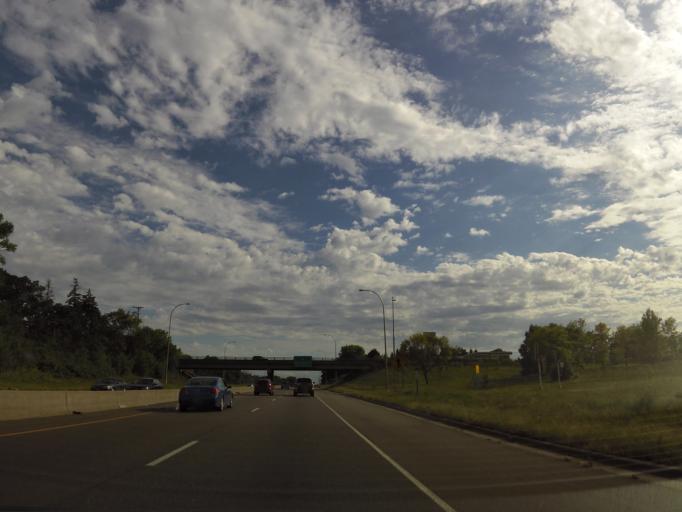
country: US
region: Minnesota
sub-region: Hennepin County
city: New Hope
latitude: 45.0706
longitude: -93.4013
